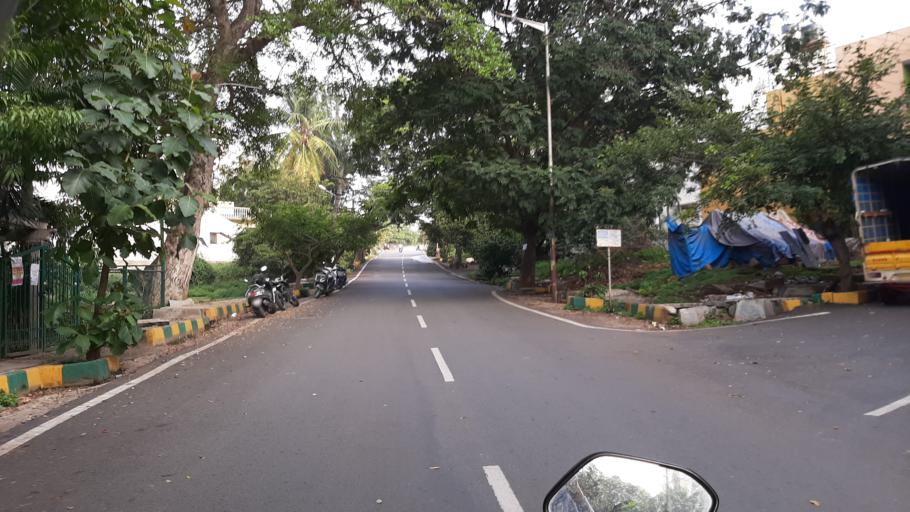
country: IN
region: Karnataka
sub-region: Bangalore Urban
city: Bangalore
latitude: 12.9771
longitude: 77.5124
